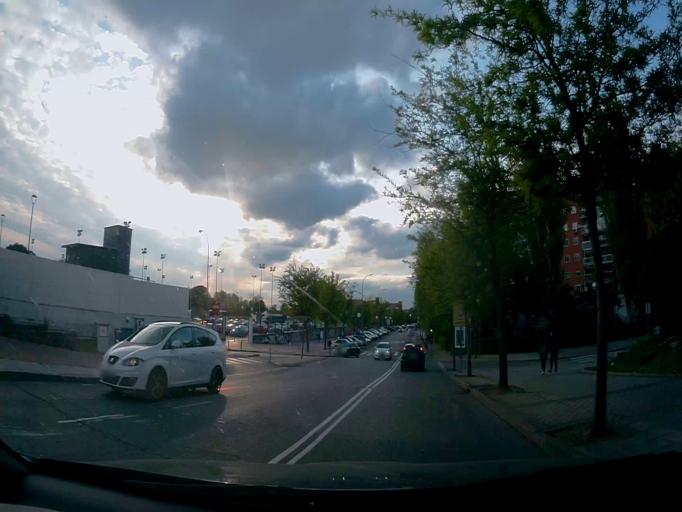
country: ES
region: Madrid
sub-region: Provincia de Madrid
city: Mostoles
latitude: 40.3190
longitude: -3.8778
